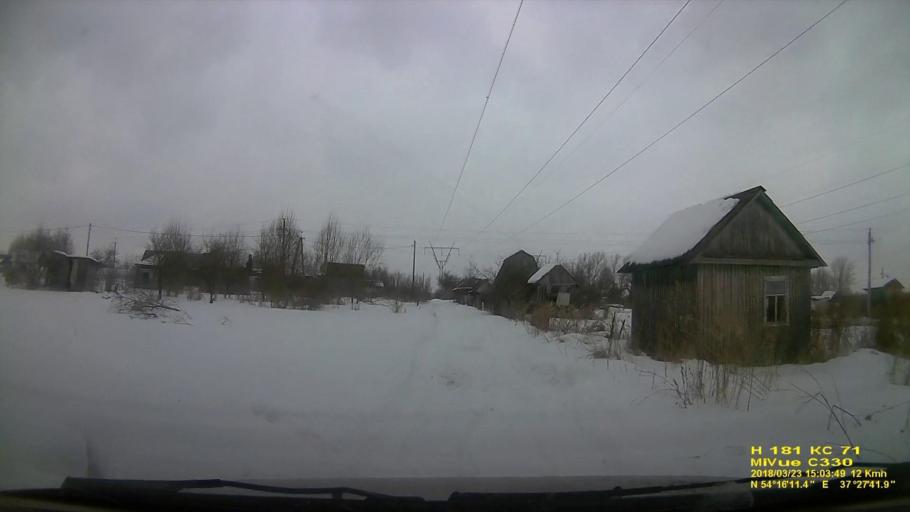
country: RU
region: Tula
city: Leninskiy
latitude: 54.2699
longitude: 37.4617
